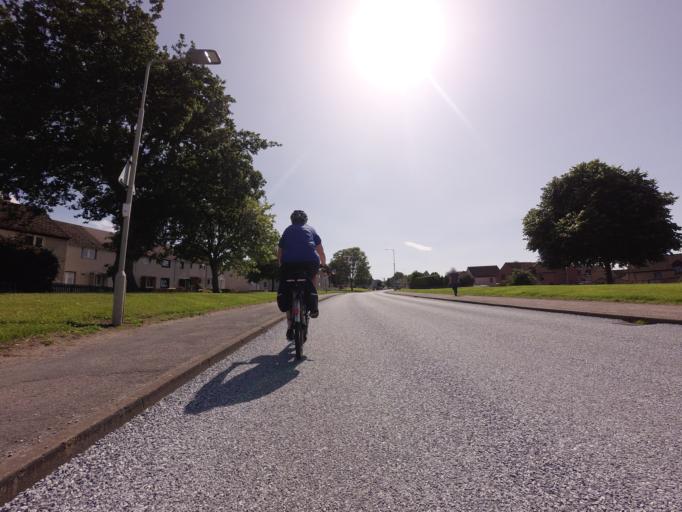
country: GB
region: Scotland
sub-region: Highland
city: Inverness
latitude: 57.4816
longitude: -4.1498
